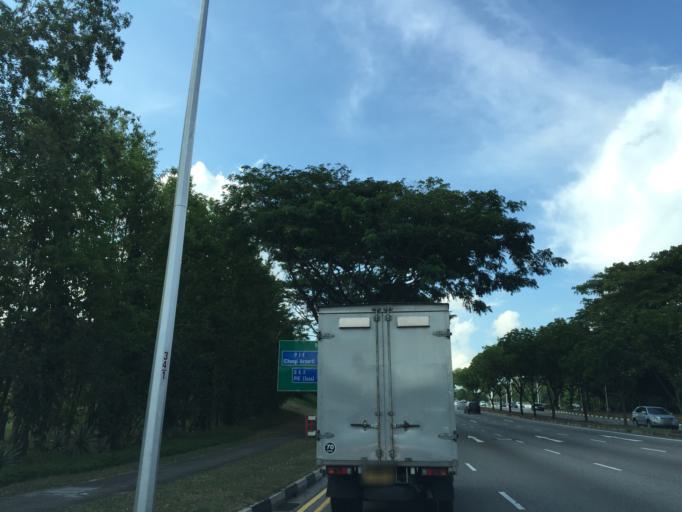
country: SG
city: Singapore
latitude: 1.3308
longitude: 103.8154
